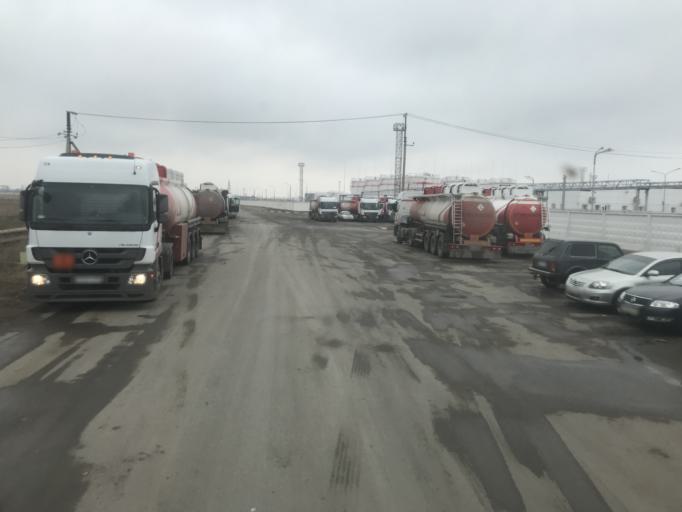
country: RU
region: Volgograd
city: Svetlyy Yar
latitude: 48.5095
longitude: 44.6400
